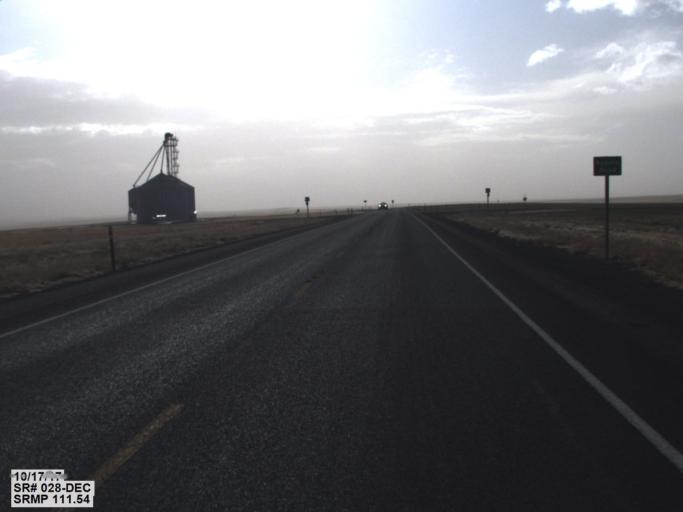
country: US
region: Washington
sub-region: Adams County
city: Ritzville
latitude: 47.4231
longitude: -118.3559
